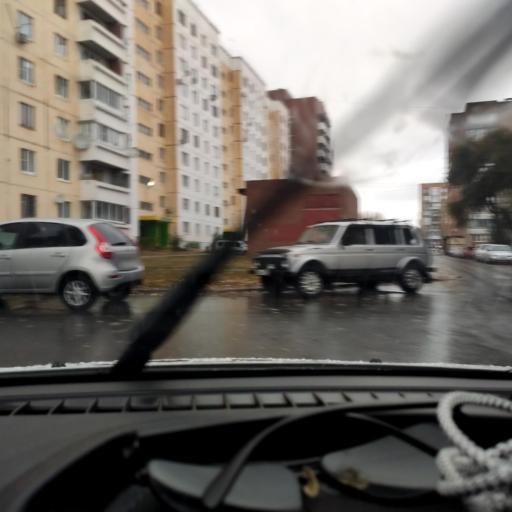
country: RU
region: Samara
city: Zhigulevsk
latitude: 53.4799
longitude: 49.4814
